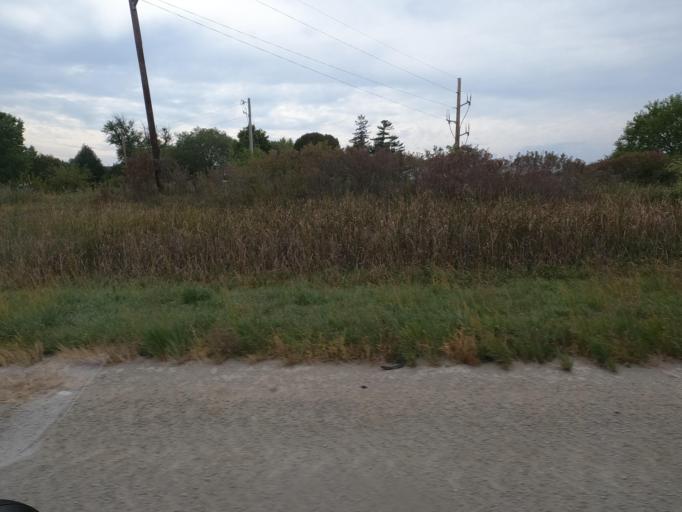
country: US
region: Iowa
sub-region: Marion County
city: Pella
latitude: 41.4077
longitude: -92.9444
